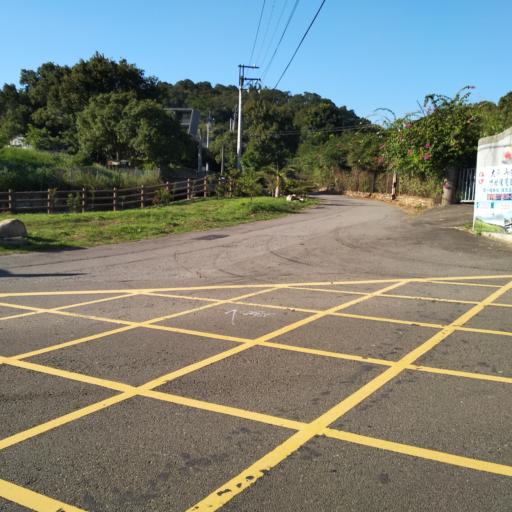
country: TW
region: Taiwan
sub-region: Hsinchu
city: Zhubei
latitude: 24.8420
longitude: 121.0613
